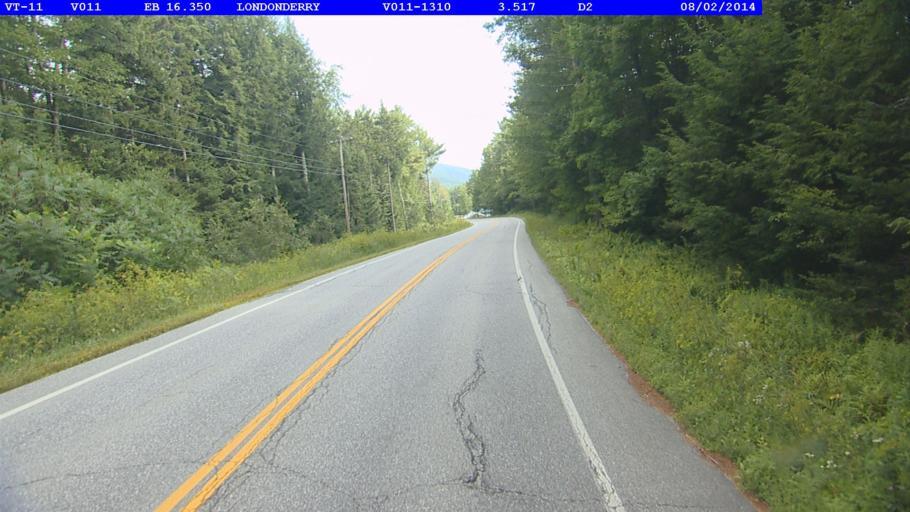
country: US
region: Vermont
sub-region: Windsor County
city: Chester
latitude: 43.2173
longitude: -72.7906
